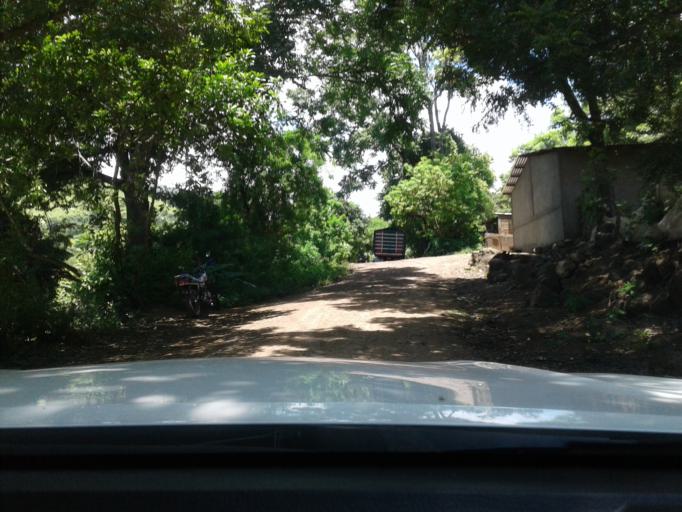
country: NI
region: Matagalpa
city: Terrabona
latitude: 12.8335
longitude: -85.9866
